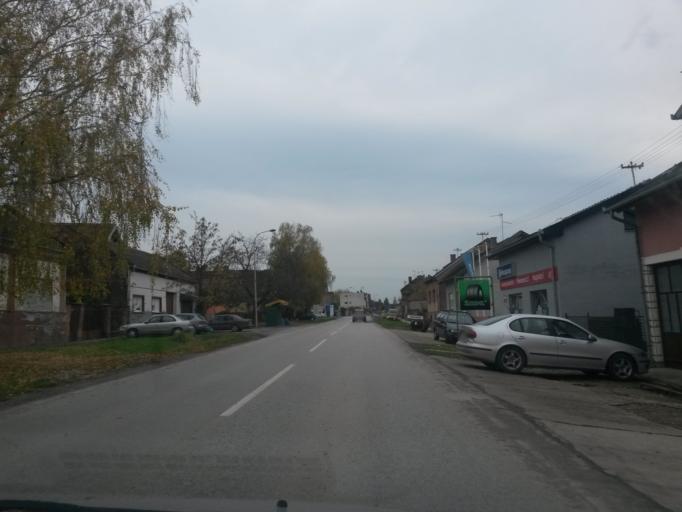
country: HR
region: Osjecko-Baranjska
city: Darda
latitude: 45.6307
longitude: 18.6874
